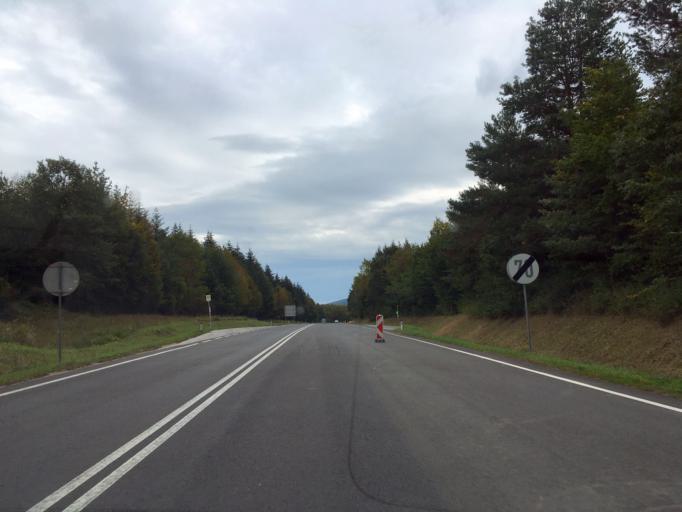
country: AT
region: Lower Austria
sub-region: Politischer Bezirk Baden
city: Heiligenkreuz
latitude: 48.0561
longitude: 16.1590
